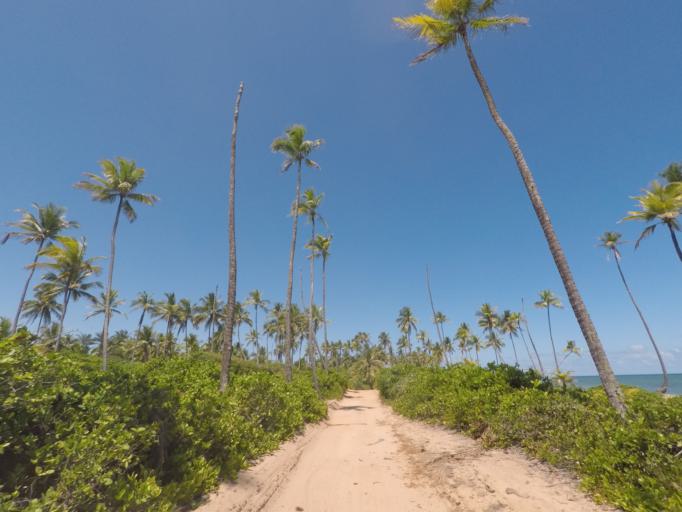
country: BR
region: Bahia
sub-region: Marau
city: Marau
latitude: -14.0166
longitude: -38.9448
